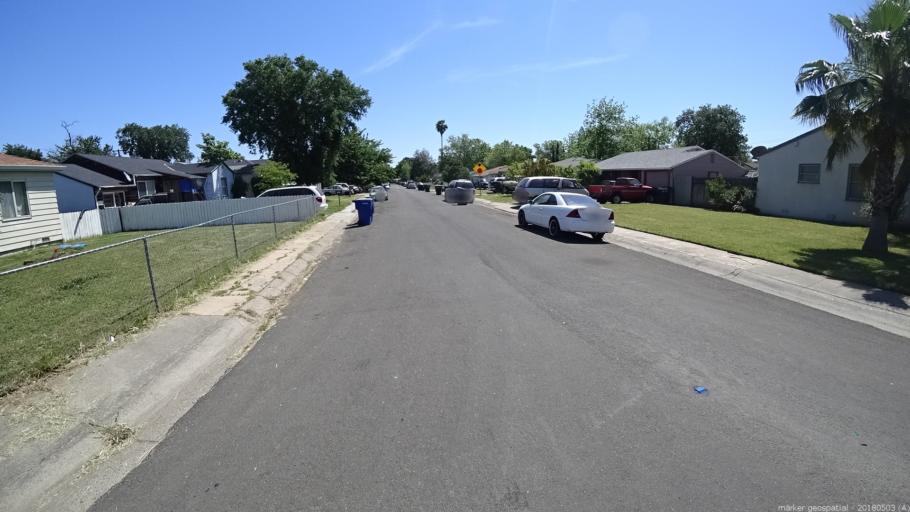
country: US
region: California
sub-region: Sacramento County
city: Arden-Arcade
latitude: 38.6319
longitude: -121.4290
